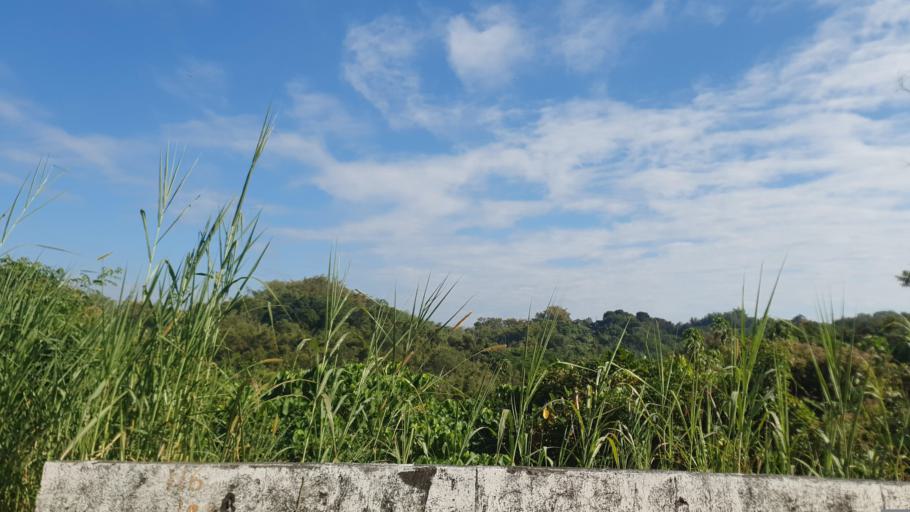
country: TW
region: Taiwan
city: Yujing
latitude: 23.0212
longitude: 120.3843
